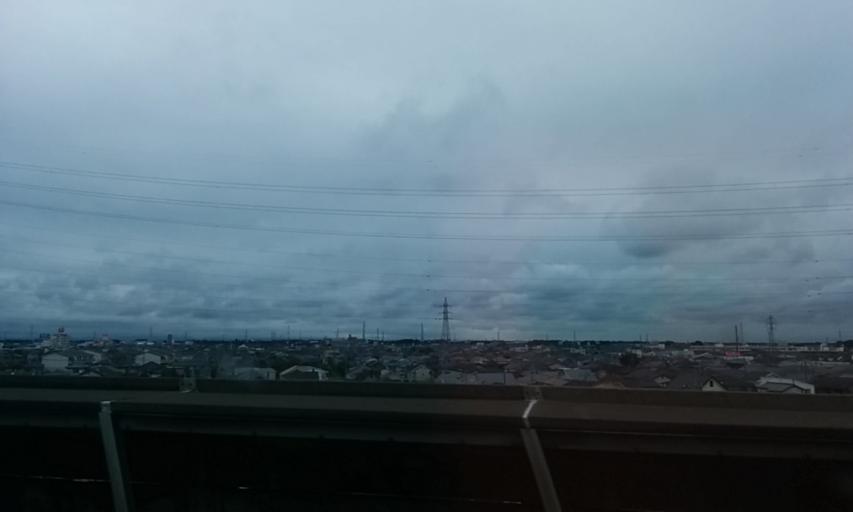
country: JP
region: Tochigi
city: Oyama
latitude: 36.2988
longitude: 139.7962
